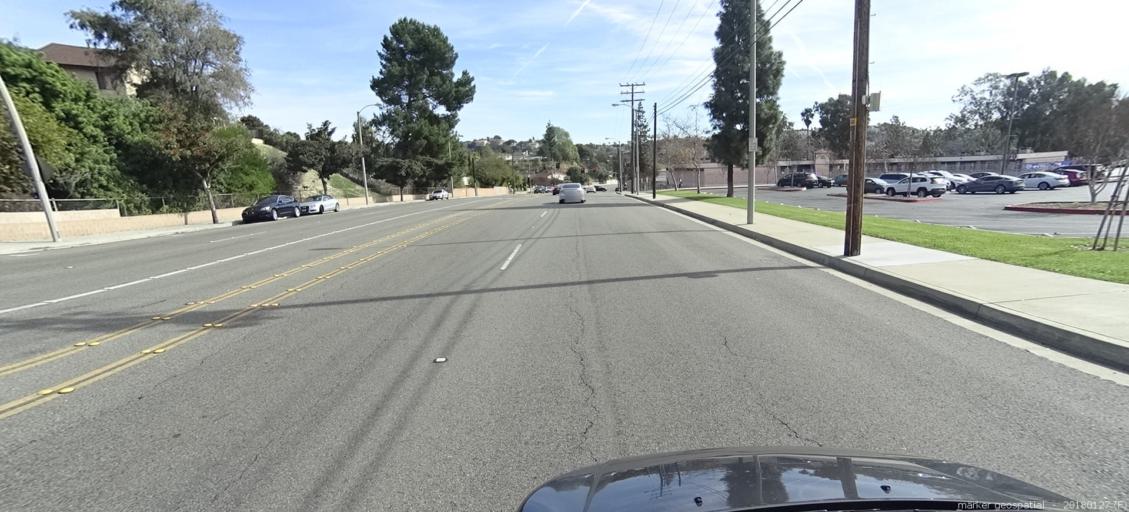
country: US
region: California
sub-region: Los Angeles County
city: Walnut
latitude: 33.9840
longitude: -117.8386
